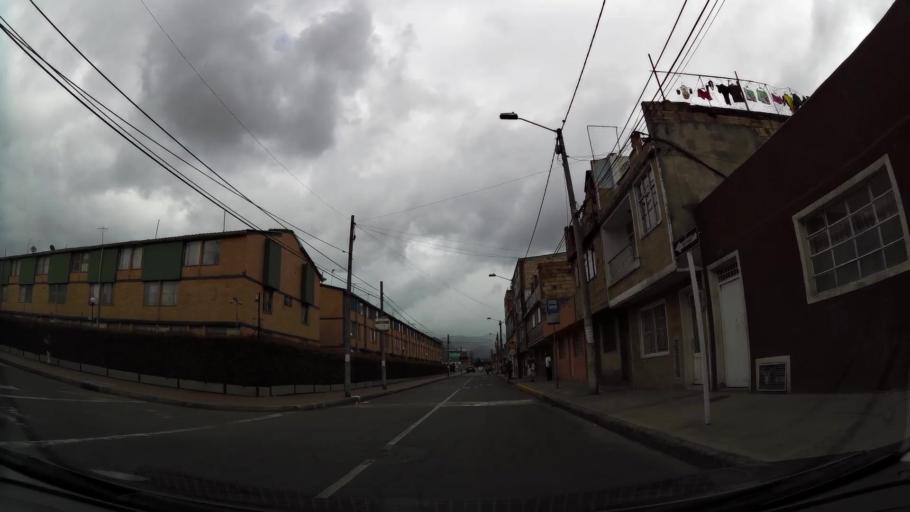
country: CO
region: Bogota D.C.
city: Barrio San Luis
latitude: 4.6979
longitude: -74.1021
